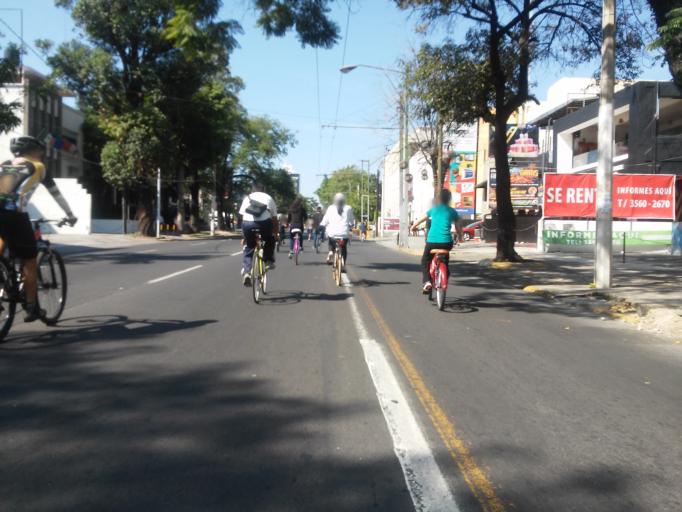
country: MX
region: Jalisco
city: Guadalajara
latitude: 20.6747
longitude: -103.3689
